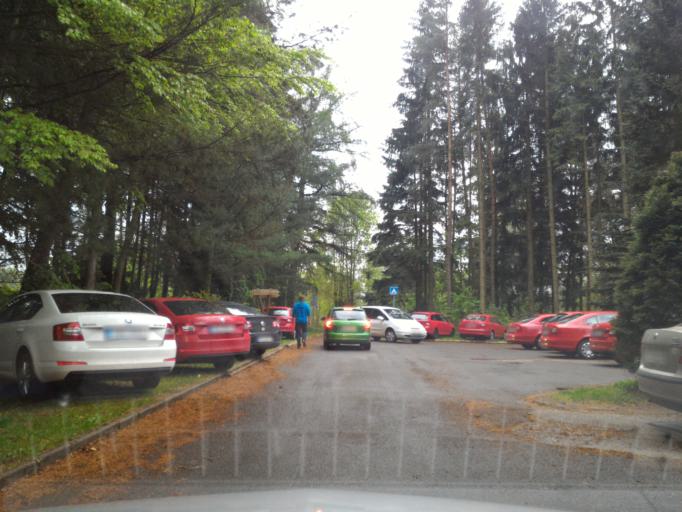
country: CZ
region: Vysocina
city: Ledec nad Sazavou
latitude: 49.6323
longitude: 15.3033
